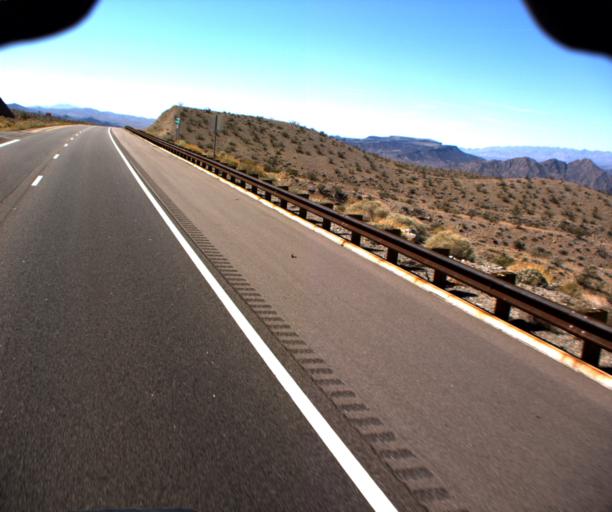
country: US
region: Nevada
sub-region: Clark County
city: Boulder City
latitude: 35.9162
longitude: -114.6300
